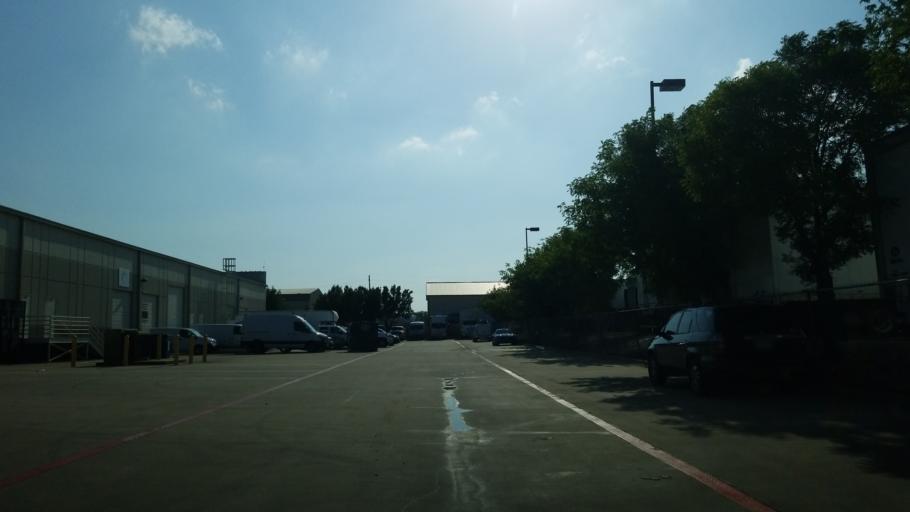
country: US
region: Texas
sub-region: Dallas County
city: Farmers Branch
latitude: 32.8746
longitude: -96.9049
